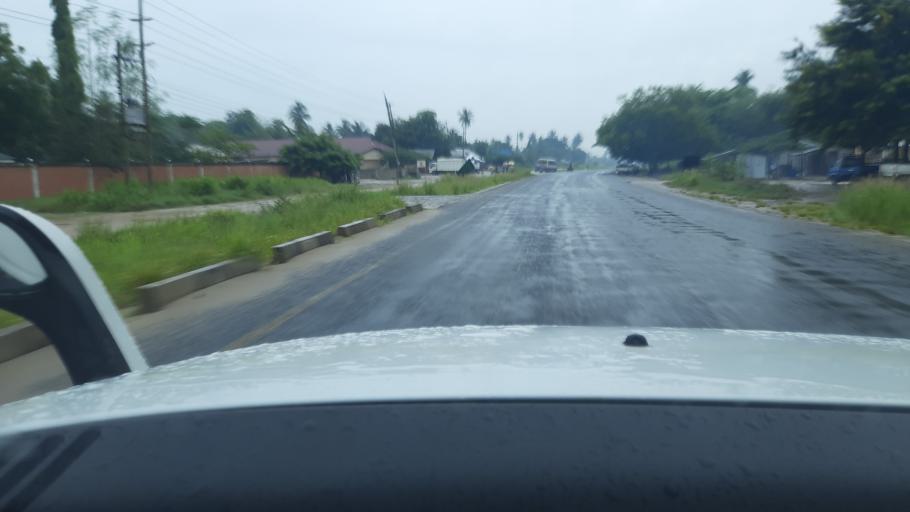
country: TZ
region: Pwani
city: Bagamoyo
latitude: -6.5095
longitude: 38.9331
